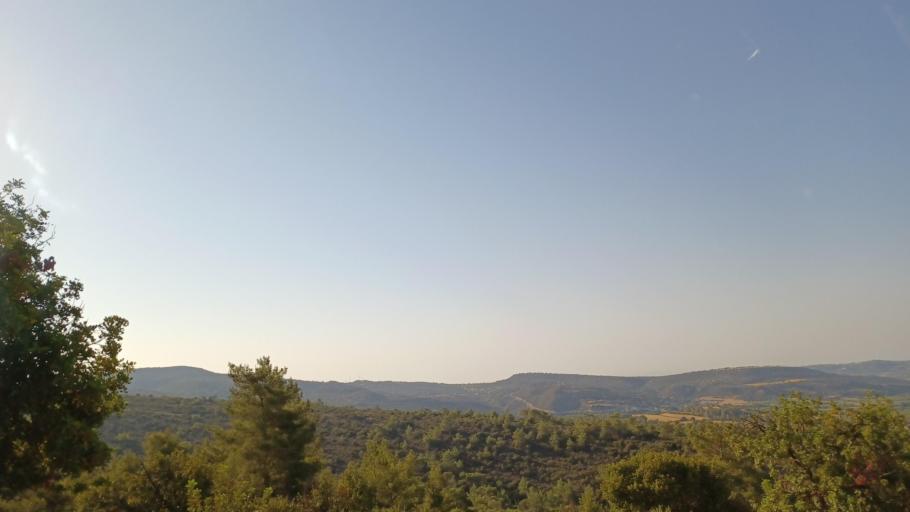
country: CY
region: Limassol
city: Pissouri
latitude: 34.7272
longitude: 32.6691
